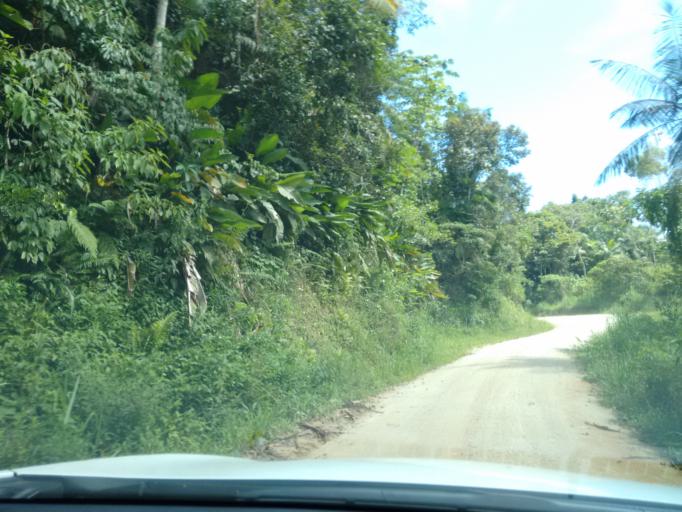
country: BR
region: Santa Catarina
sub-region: Pomerode
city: Pomerode
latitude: -26.7116
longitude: -49.0933
